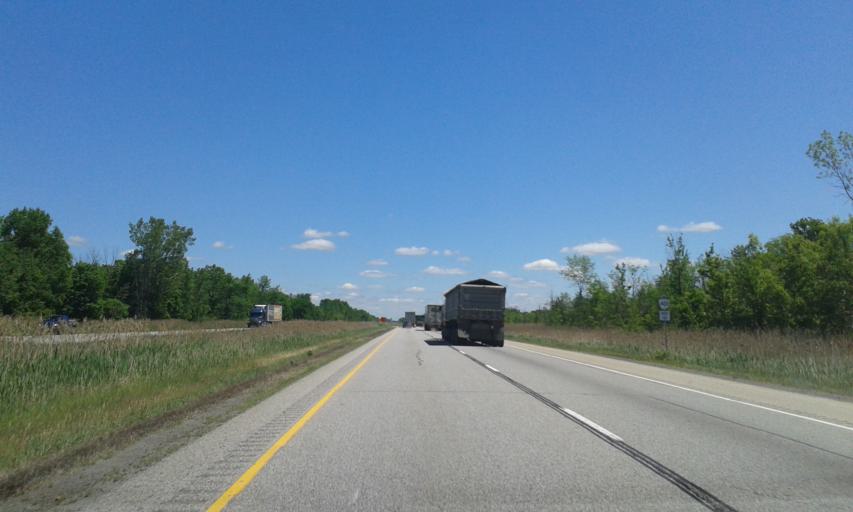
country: US
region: New York
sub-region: St. Lawrence County
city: Norfolk
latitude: 44.9190
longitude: -75.1925
